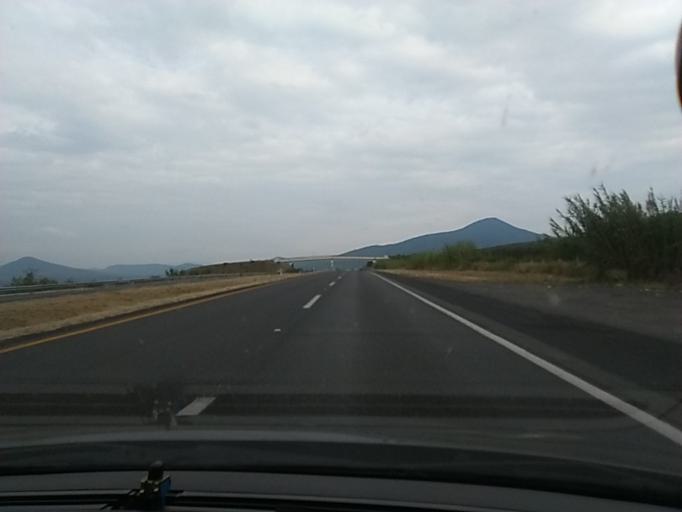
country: MX
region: Michoacan
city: Panindicuaro de la Reforma
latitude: 19.9832
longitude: -101.7896
